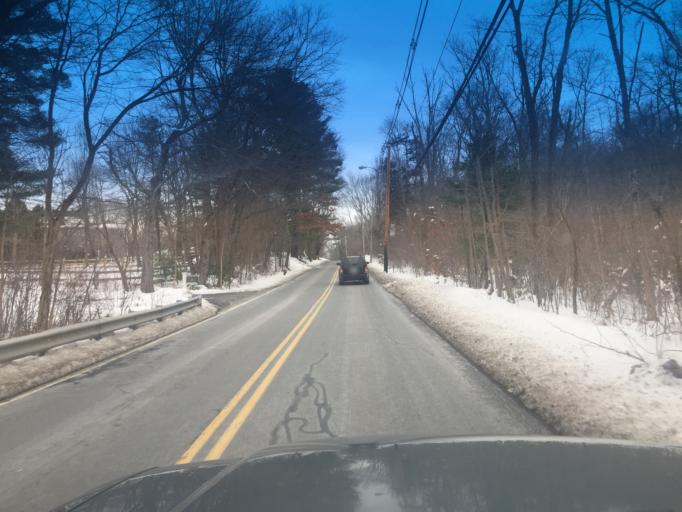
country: US
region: Massachusetts
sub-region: Norfolk County
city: Norfolk
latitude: 42.1159
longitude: -71.2920
